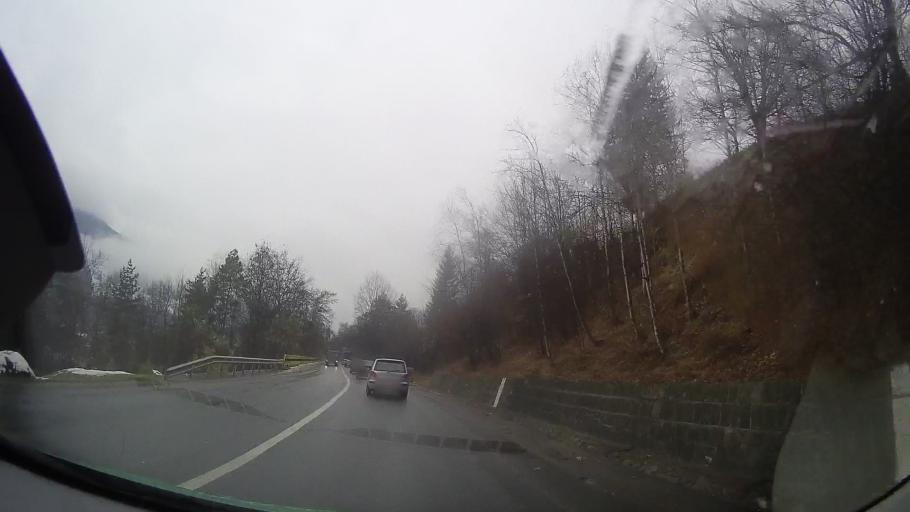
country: RO
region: Neamt
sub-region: Comuna Bicaz
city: Dodeni
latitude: 46.9017
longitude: 26.1172
